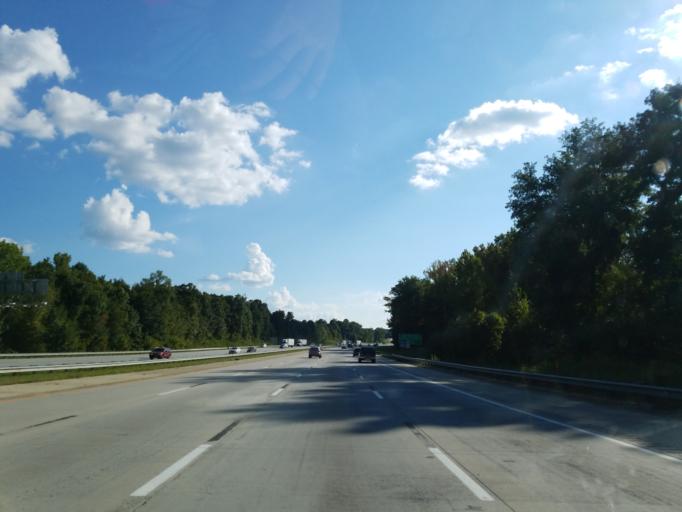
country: US
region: North Carolina
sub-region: Rowan County
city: East Spencer
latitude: 35.6868
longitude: -80.4049
